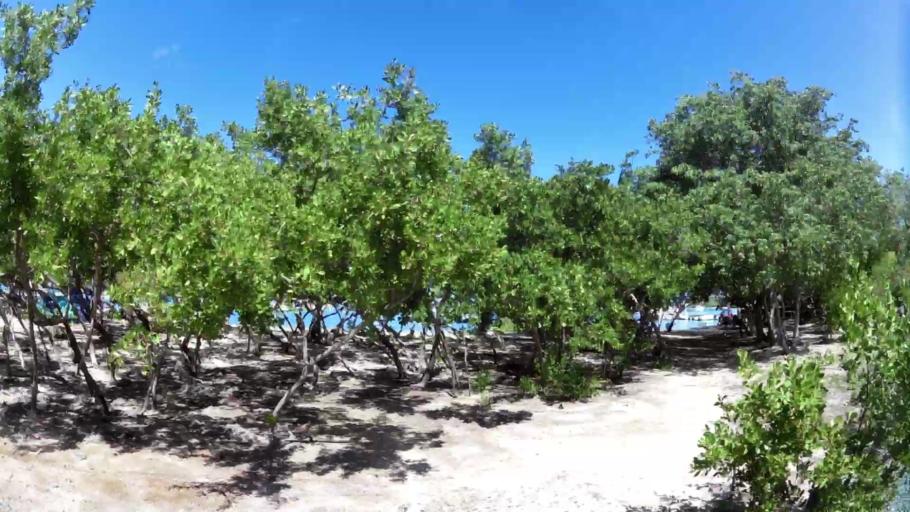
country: VG
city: Tortola
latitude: 18.4445
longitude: -64.5337
